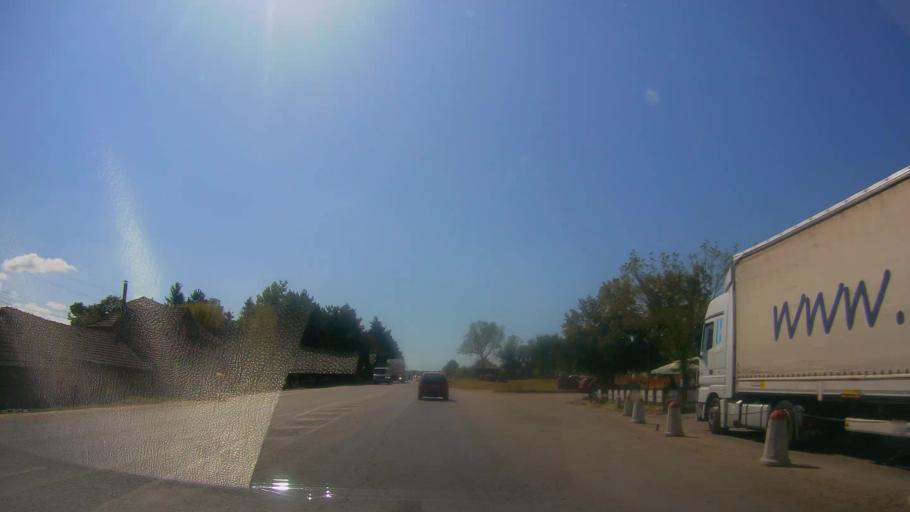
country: BG
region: Veliko Turnovo
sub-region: Obshtina Gorna Oryakhovitsa
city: Purvomaytsi
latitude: 43.2660
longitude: 25.6434
